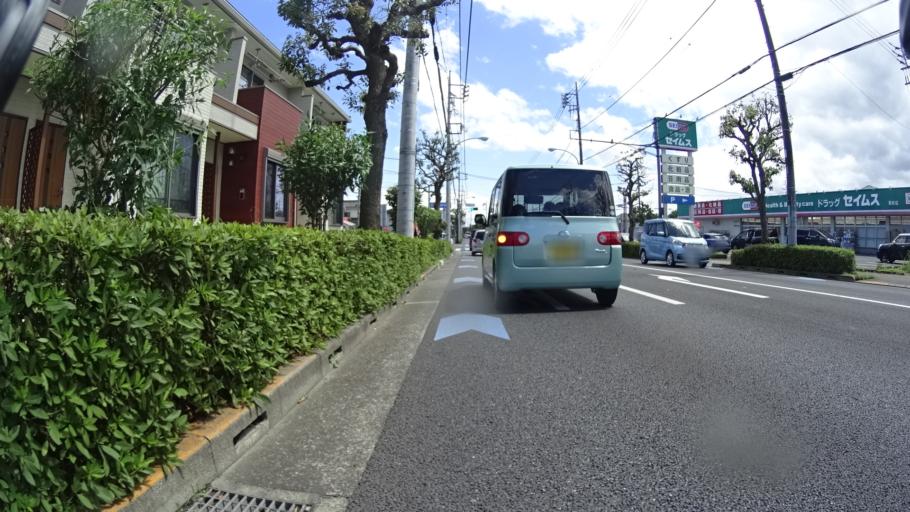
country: JP
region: Tokyo
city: Fussa
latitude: 35.7696
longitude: 139.3052
